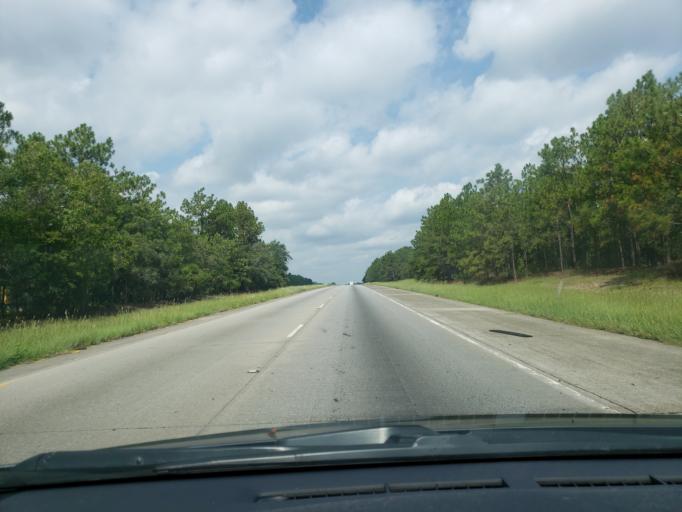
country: US
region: Georgia
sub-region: Emanuel County
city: Swainsboro
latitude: 32.4155
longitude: -82.3800
